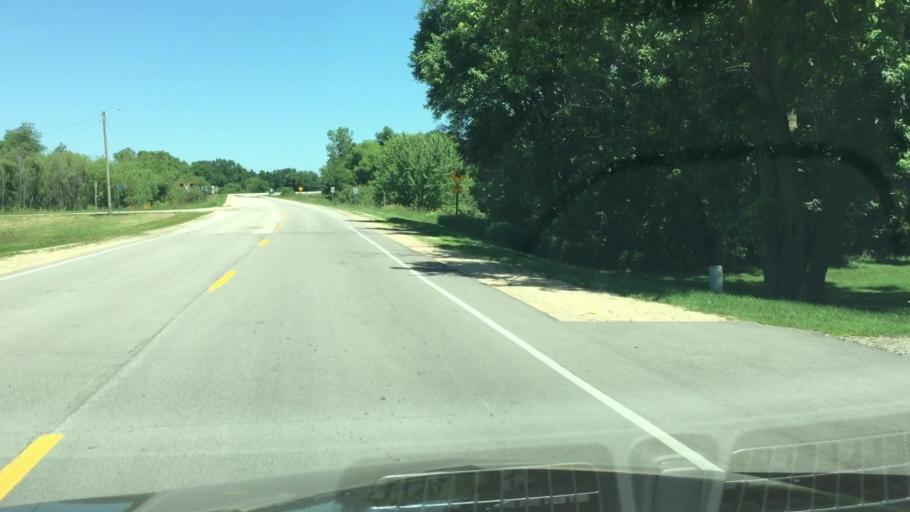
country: US
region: Iowa
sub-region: Cedar County
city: Mechanicsville
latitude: 42.0016
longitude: -91.1419
